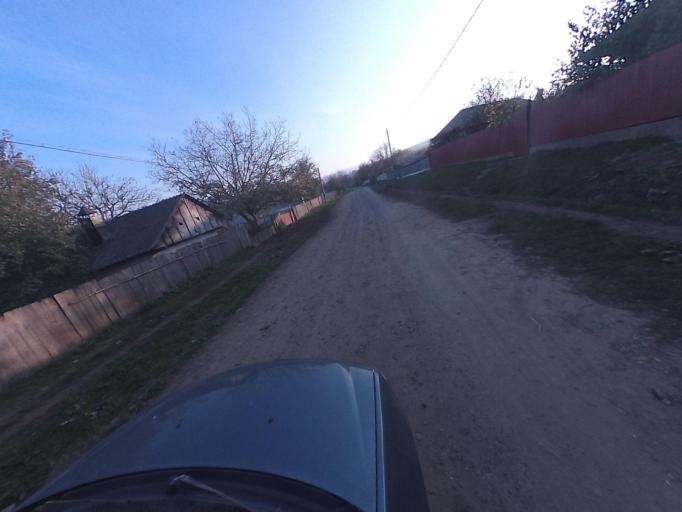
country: RO
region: Vaslui
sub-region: Comuna Bacesti
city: Bacesti
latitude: 46.8074
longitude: 27.2251
